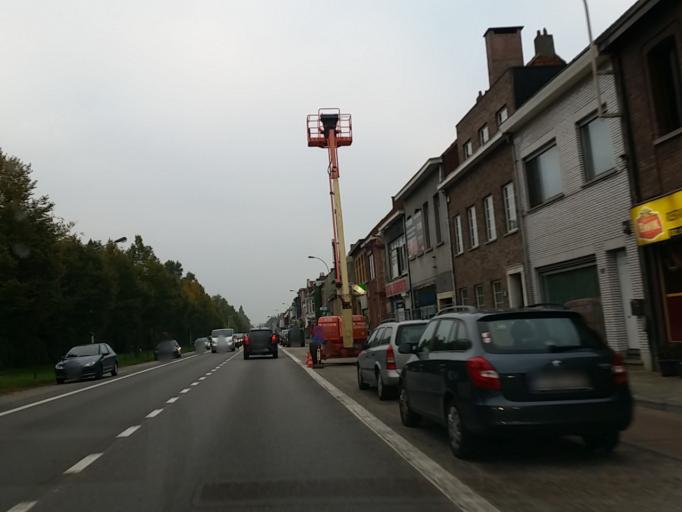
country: BE
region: Flanders
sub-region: Provincie Antwerpen
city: Kapellen
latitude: 51.2785
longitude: 4.4538
